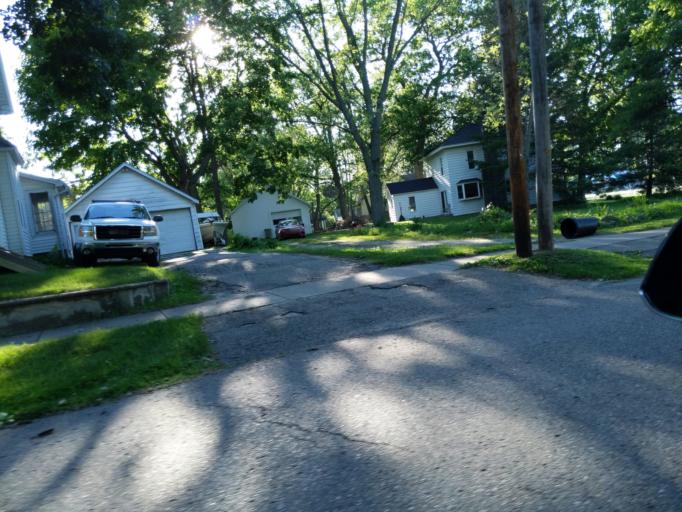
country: US
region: Michigan
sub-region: Ingham County
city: Stockbridge
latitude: 42.4521
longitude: -84.1845
